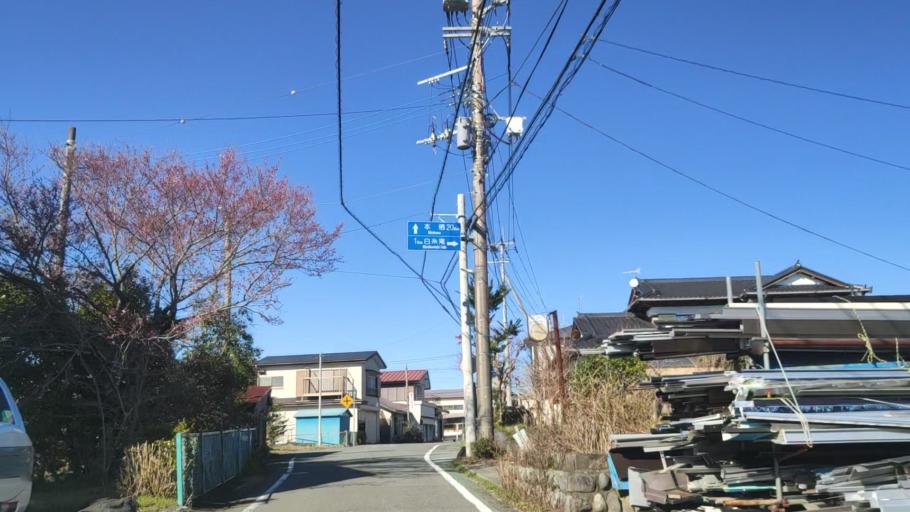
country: JP
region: Shizuoka
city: Fujinomiya
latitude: 35.3105
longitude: 138.5762
